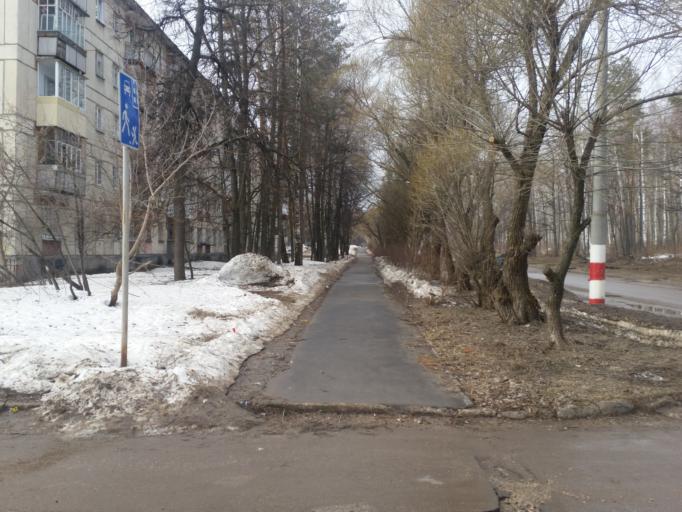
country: RU
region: Ulyanovsk
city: Dimitrovgrad
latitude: 54.2387
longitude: 49.5527
